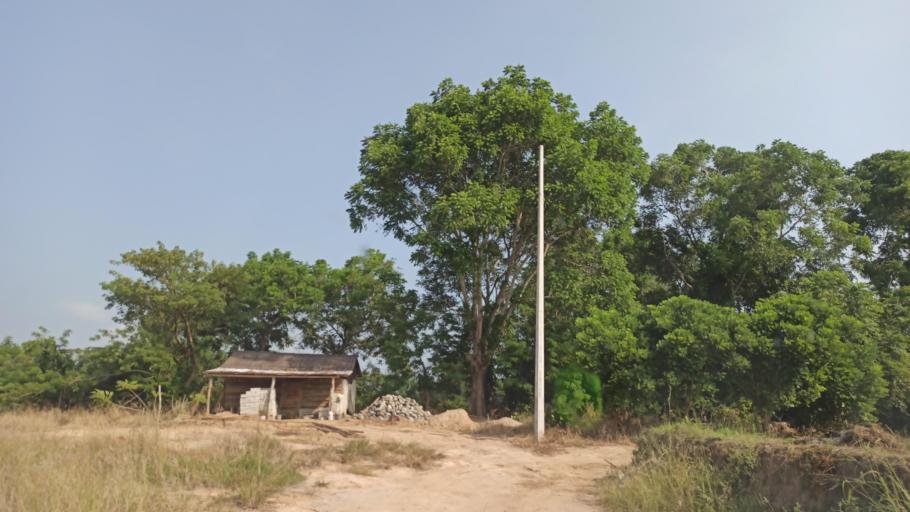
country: MX
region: Veracruz
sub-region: Martinez de la Torre
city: El Progreso
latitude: 20.1505
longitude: -97.0685
